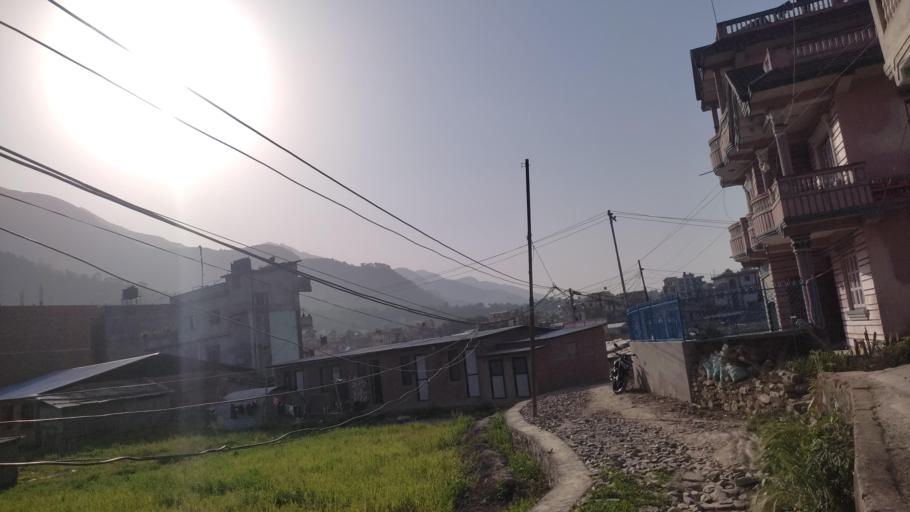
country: NP
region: Central Region
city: Kirtipur
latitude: 27.6601
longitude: 85.2698
